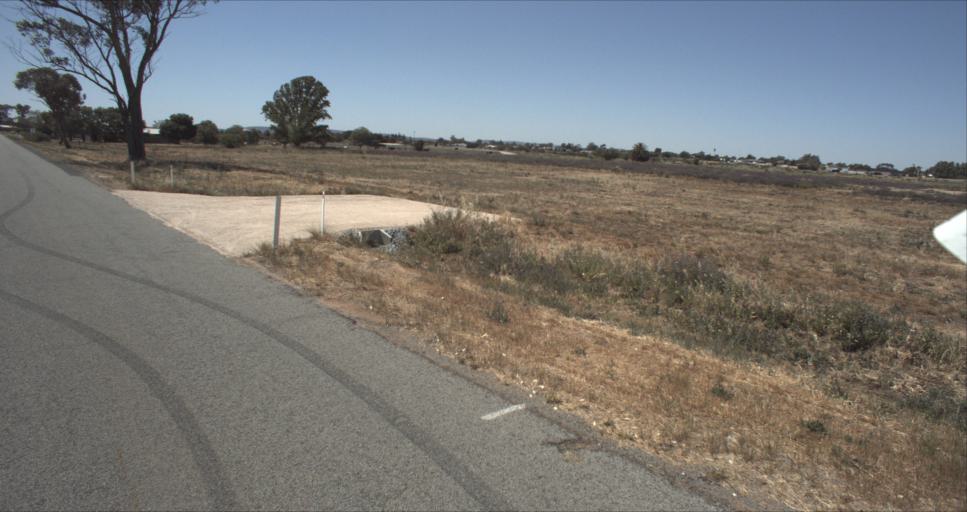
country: AU
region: New South Wales
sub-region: Leeton
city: Leeton
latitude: -34.5368
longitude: 146.3962
